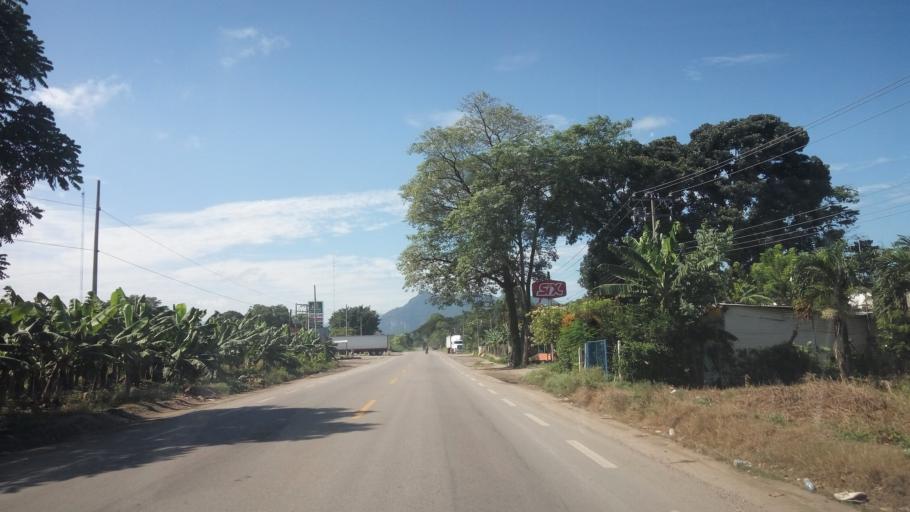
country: MX
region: Tabasco
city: Teapa
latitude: 17.5928
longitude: -92.9650
